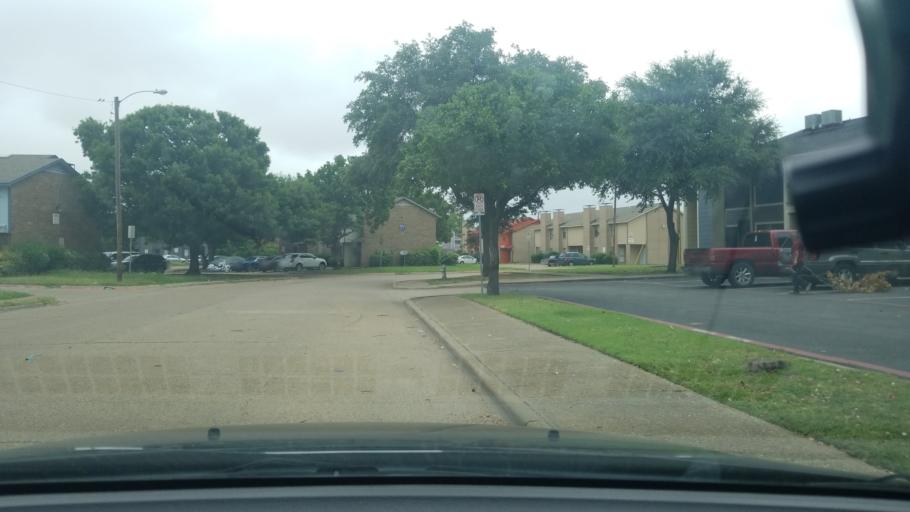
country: US
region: Texas
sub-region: Dallas County
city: Balch Springs
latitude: 32.7825
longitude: -96.6863
